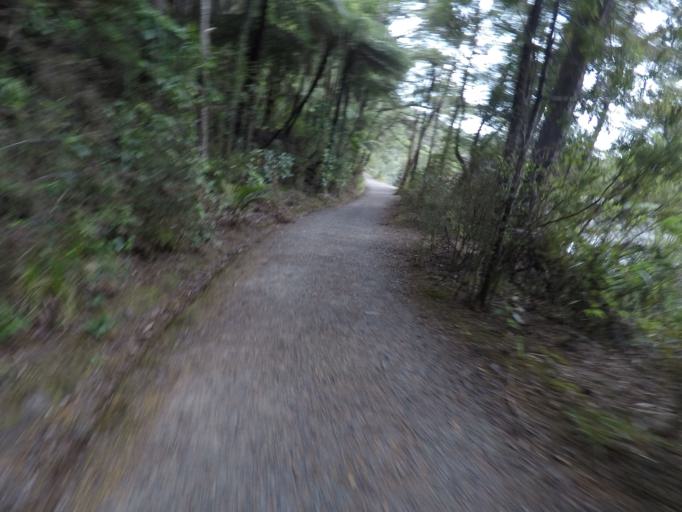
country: NZ
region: Northland
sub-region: Whangarei
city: Whangarei
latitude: -35.7117
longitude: 174.3302
